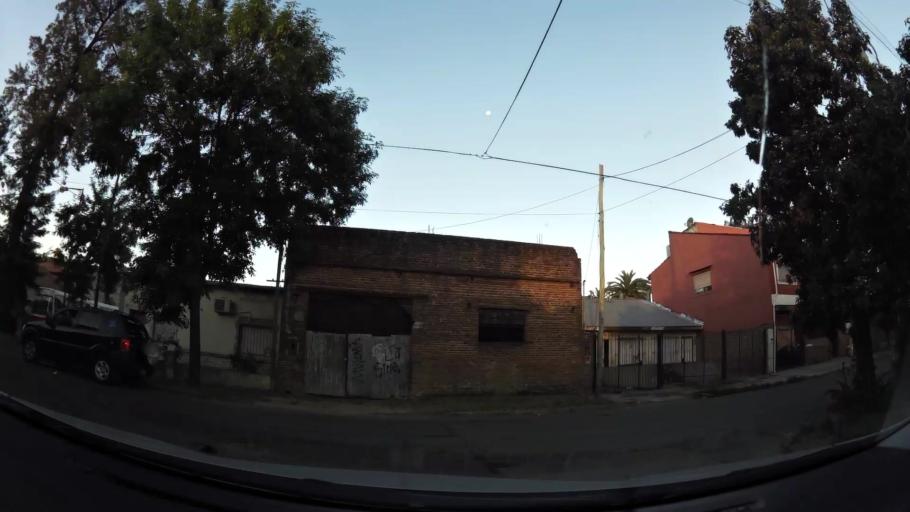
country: AR
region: Buenos Aires
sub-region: Partido de Tigre
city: Tigre
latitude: -34.4390
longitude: -58.5703
